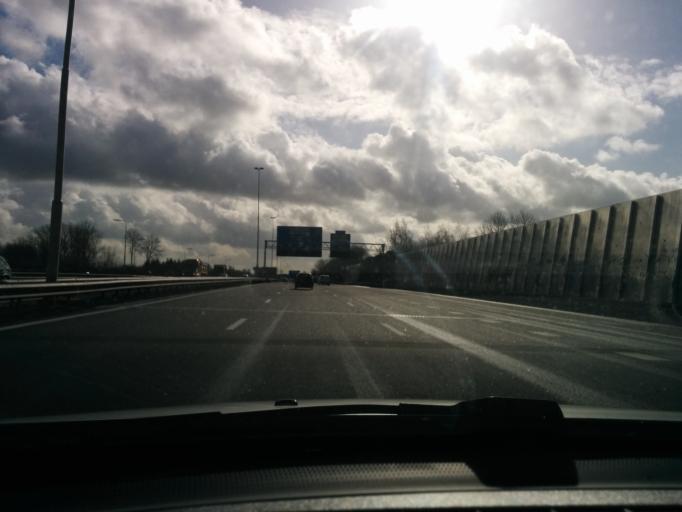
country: NL
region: Utrecht
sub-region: Gemeente De Bilt
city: De Bilt
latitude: 52.1155
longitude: 5.1471
